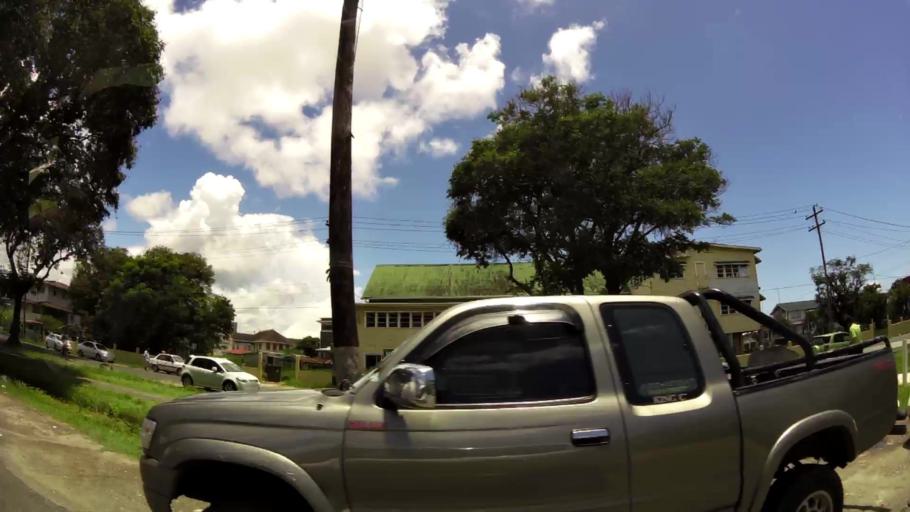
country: GY
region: Demerara-Mahaica
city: Georgetown
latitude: 6.8141
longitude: -58.1631
